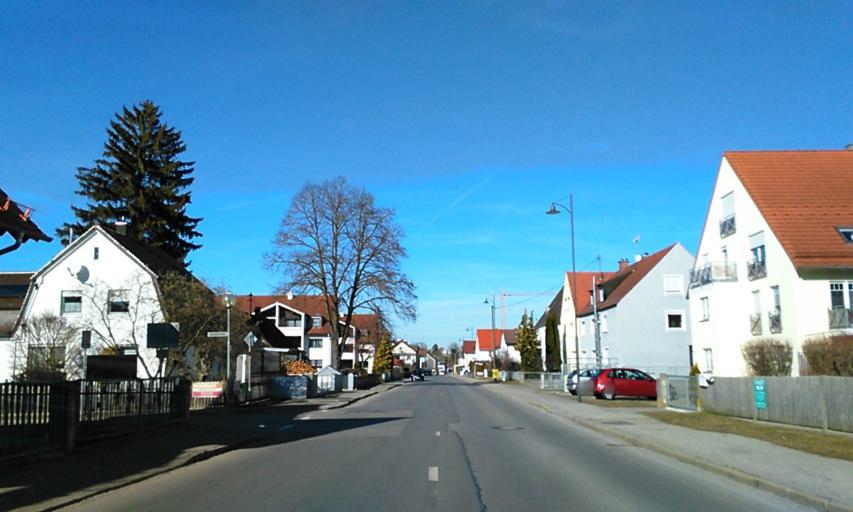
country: DE
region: Bavaria
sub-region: Swabia
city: Mering
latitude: 48.2595
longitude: 10.9852
